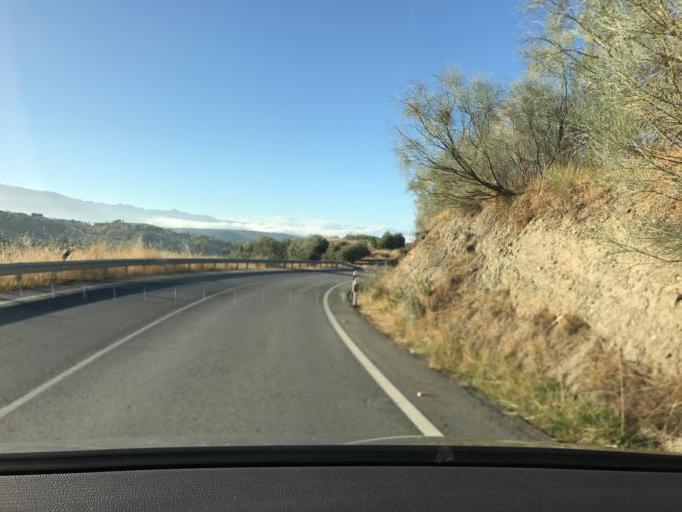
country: ES
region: Andalusia
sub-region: Provincia de Granada
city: Viznar
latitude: 37.2191
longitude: -3.5635
